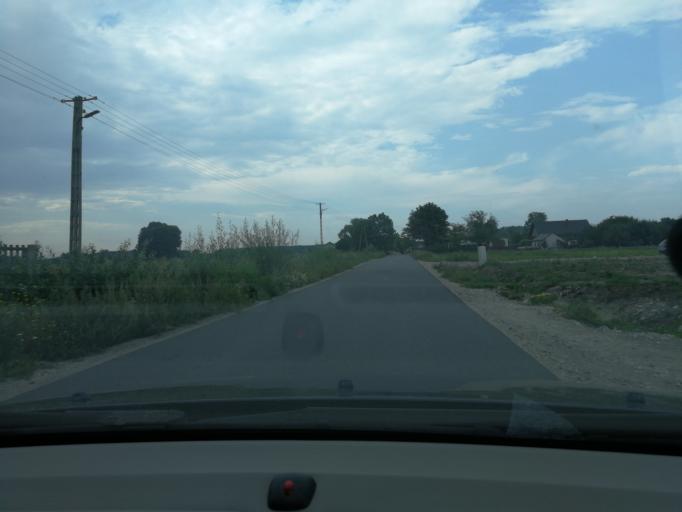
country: PL
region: Masovian Voivodeship
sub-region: Powiat grodziski
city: Grodzisk Mazowiecki
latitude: 52.1048
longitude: 20.5555
